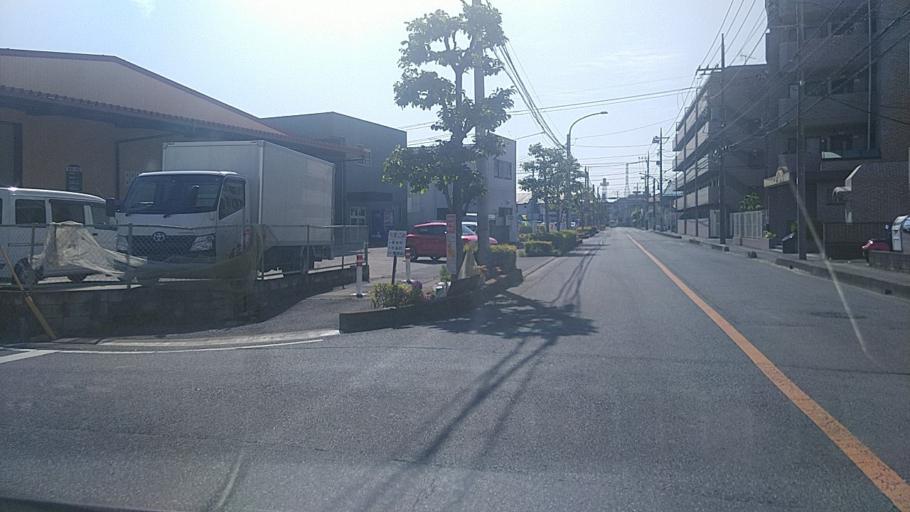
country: JP
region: Saitama
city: Koshigaya
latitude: 35.8800
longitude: 139.7487
